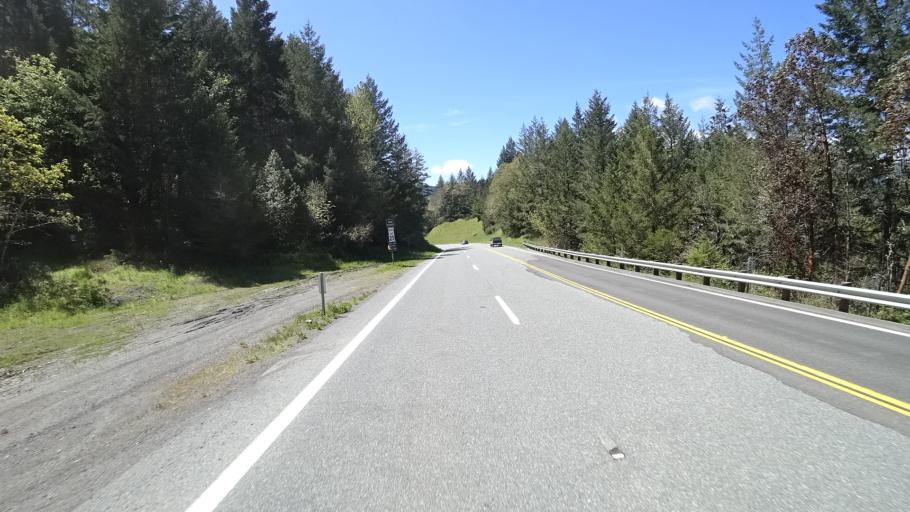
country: US
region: California
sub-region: Humboldt County
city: Willow Creek
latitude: 40.9132
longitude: -123.8069
